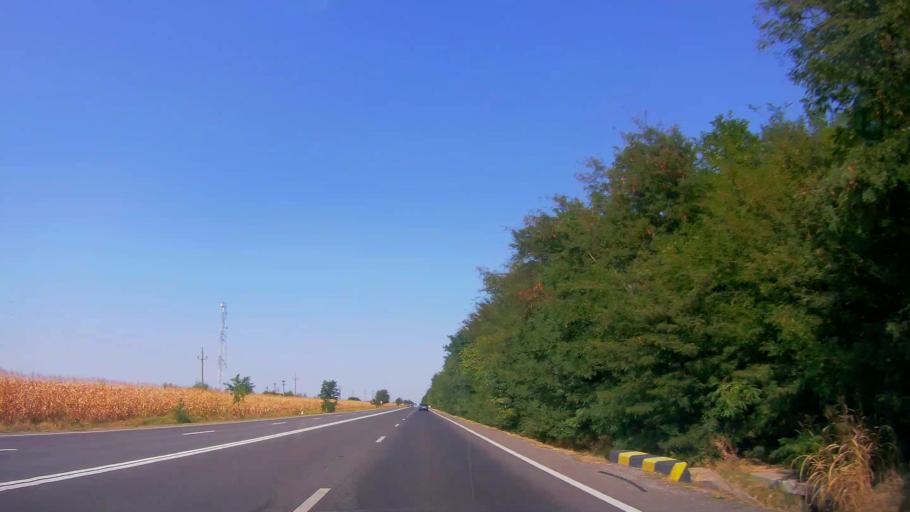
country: RO
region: Giurgiu
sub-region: Comuna Daia
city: Plopsoru
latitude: 44.0381
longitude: 25.9758
